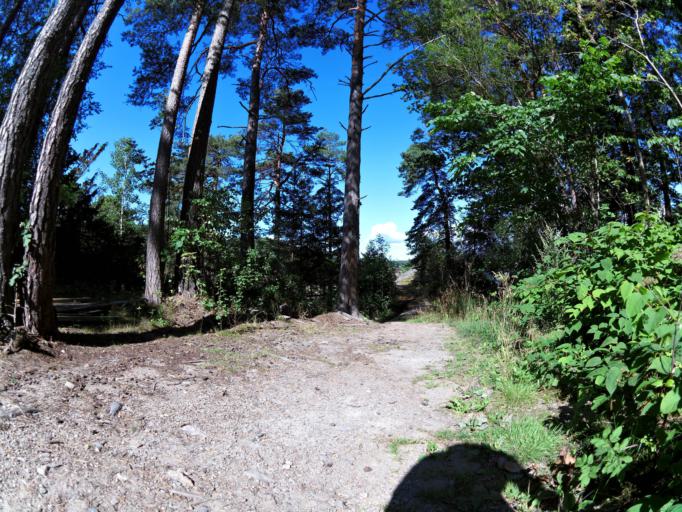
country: NO
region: Ostfold
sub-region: Fredrikstad
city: Fredrikstad
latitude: 59.1765
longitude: 10.8551
